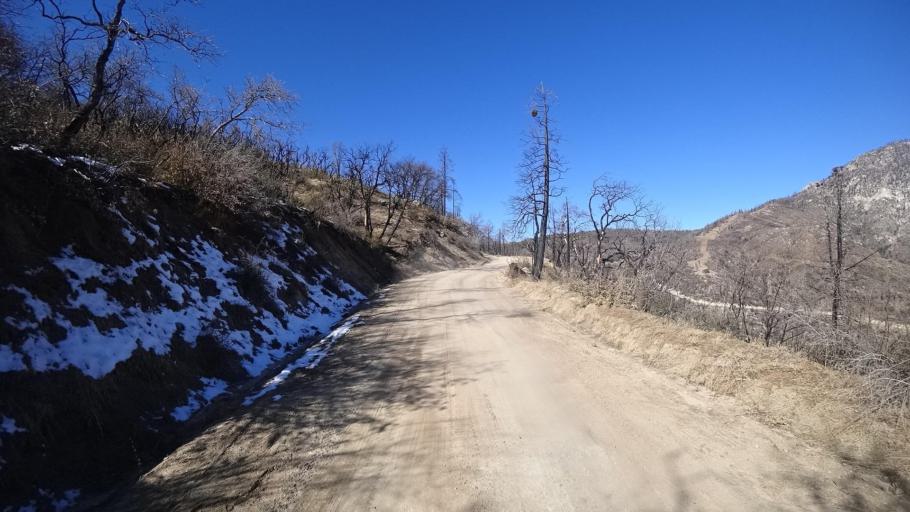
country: US
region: California
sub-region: Kern County
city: Alta Sierra
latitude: 35.7163
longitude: -118.5269
